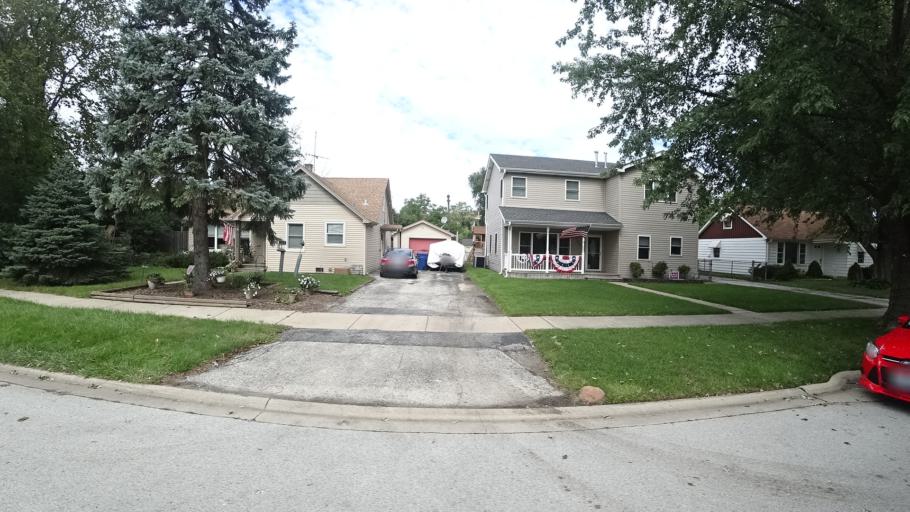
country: US
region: Illinois
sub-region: Cook County
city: Burbank
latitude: 41.7184
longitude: -87.7957
